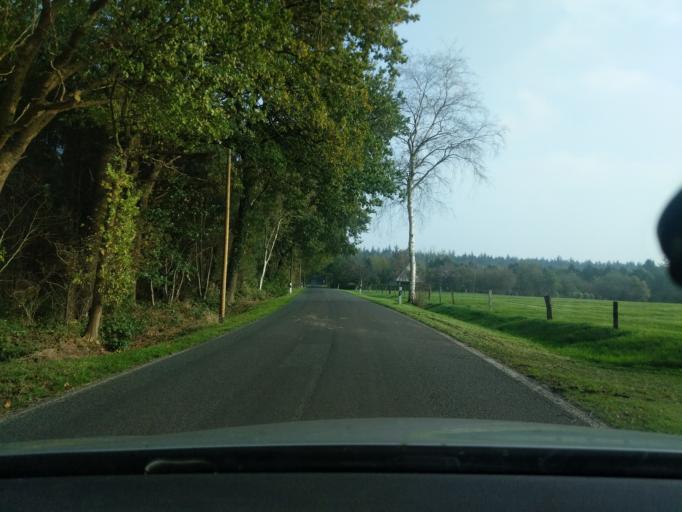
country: DE
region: Lower Saxony
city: Wanna
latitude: 53.7501
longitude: 8.7442
